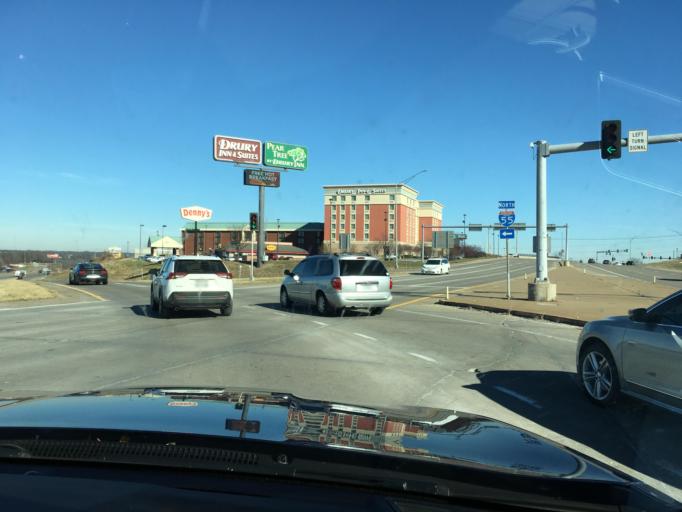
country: US
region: Missouri
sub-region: Jefferson County
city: Arnold
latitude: 38.4428
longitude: -90.3788
